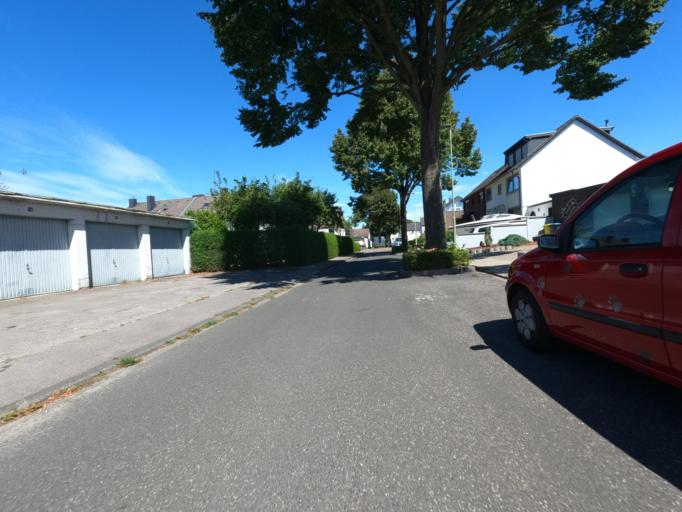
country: DE
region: North Rhine-Westphalia
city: Baesweiler
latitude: 50.9048
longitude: 6.1701
